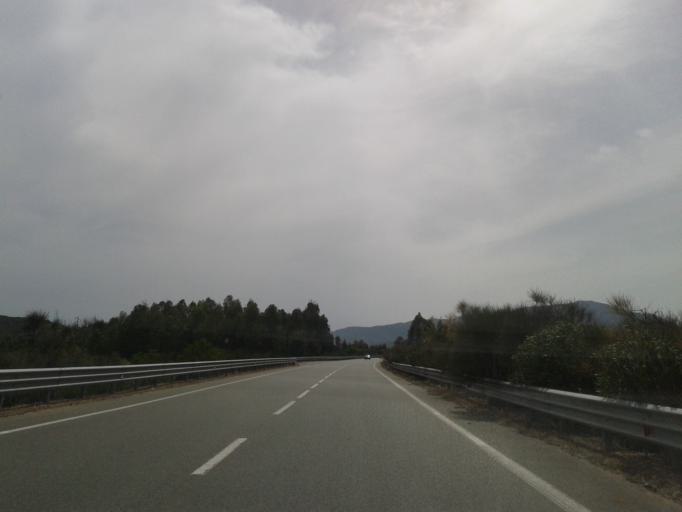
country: IT
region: Sardinia
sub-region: Provincia di Cagliari
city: Olia Speciosa
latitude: 39.2615
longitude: 9.5343
